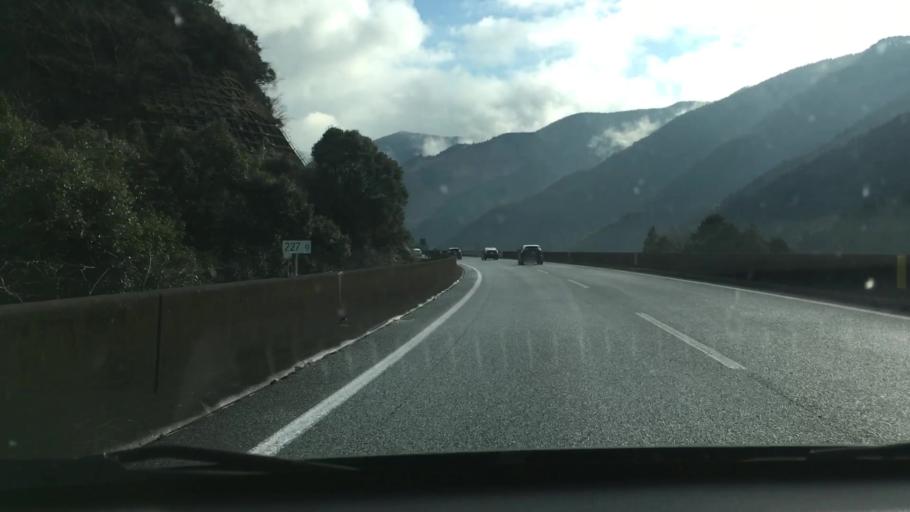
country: JP
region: Kumamoto
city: Yatsushiro
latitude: 32.4128
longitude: 130.6955
